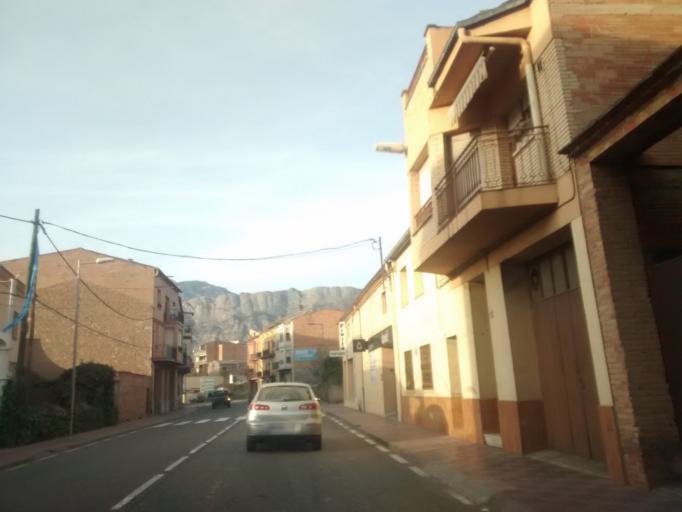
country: ES
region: Catalonia
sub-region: Provincia de Lleida
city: Oliana
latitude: 42.0693
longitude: 1.3129
